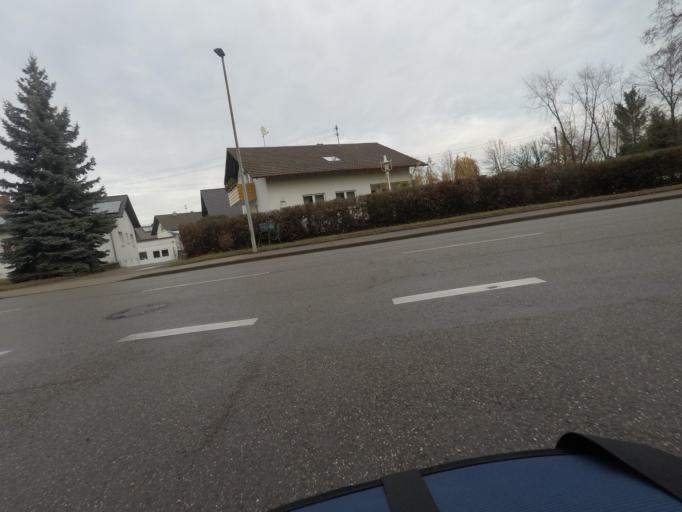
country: DE
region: Baden-Wuerttemberg
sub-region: Karlsruhe Region
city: Rheinau
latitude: 48.8583
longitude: 8.1615
